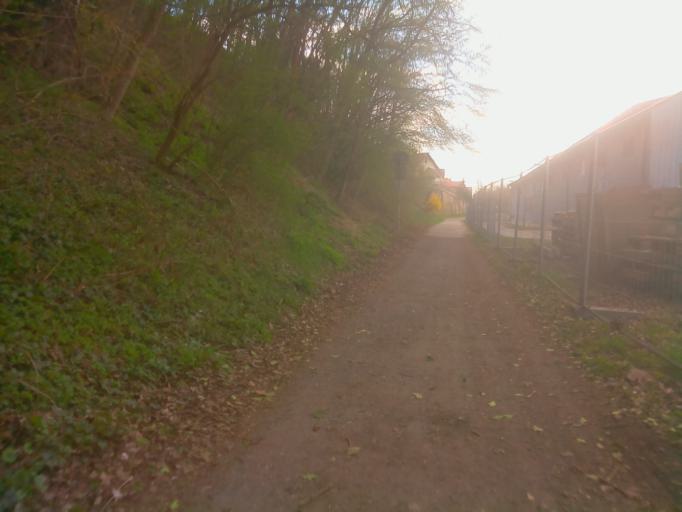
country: DE
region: Thuringia
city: Kahla
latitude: 50.8034
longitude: 11.5948
